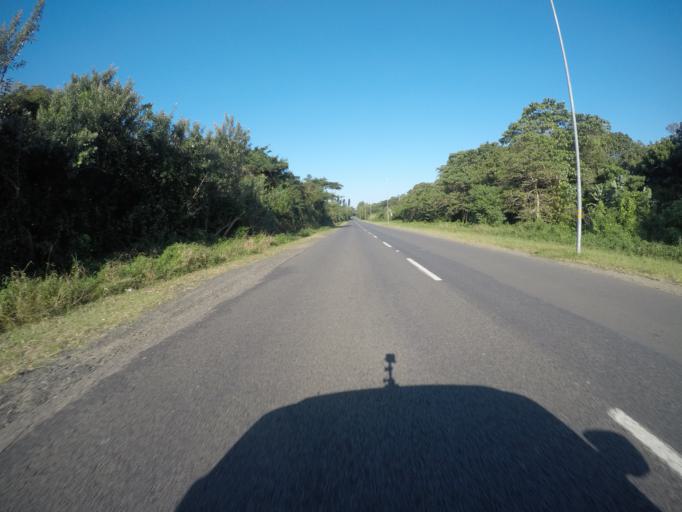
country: ZA
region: KwaZulu-Natal
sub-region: uThungulu District Municipality
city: Richards Bay
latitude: -28.7898
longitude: 32.0890
